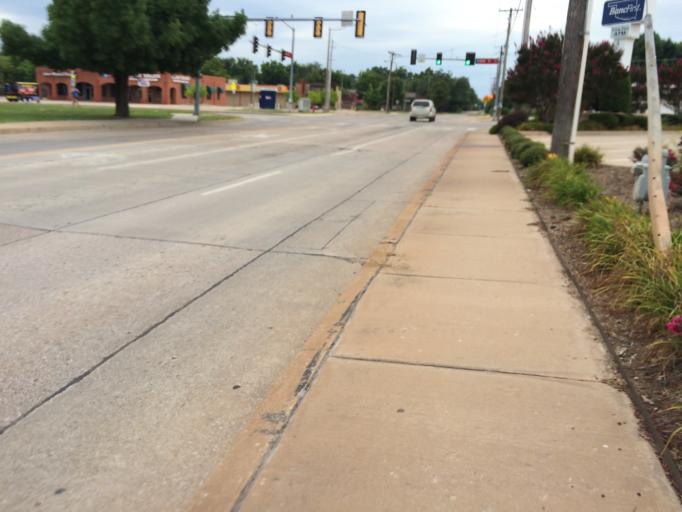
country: US
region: Oklahoma
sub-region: Cleveland County
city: Norman
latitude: 35.2190
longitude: -97.4591
